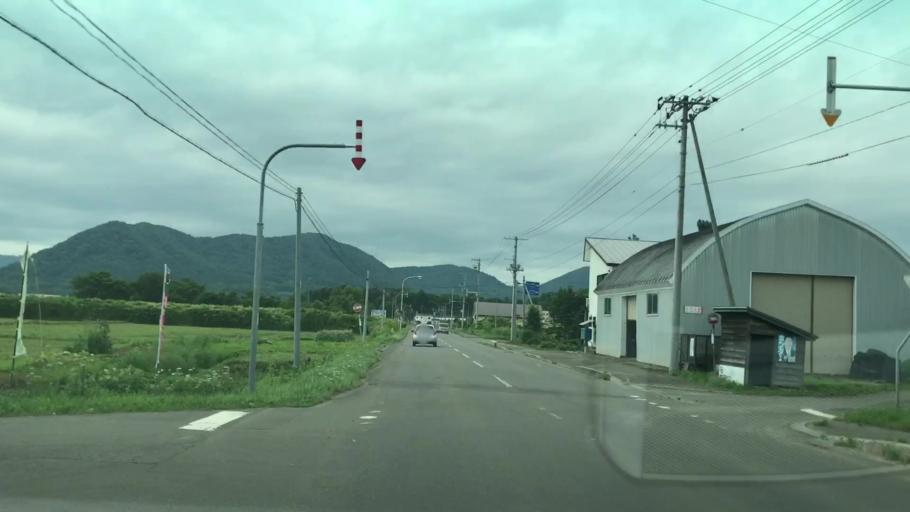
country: JP
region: Hokkaido
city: Yoichi
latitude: 43.0928
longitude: 140.8187
